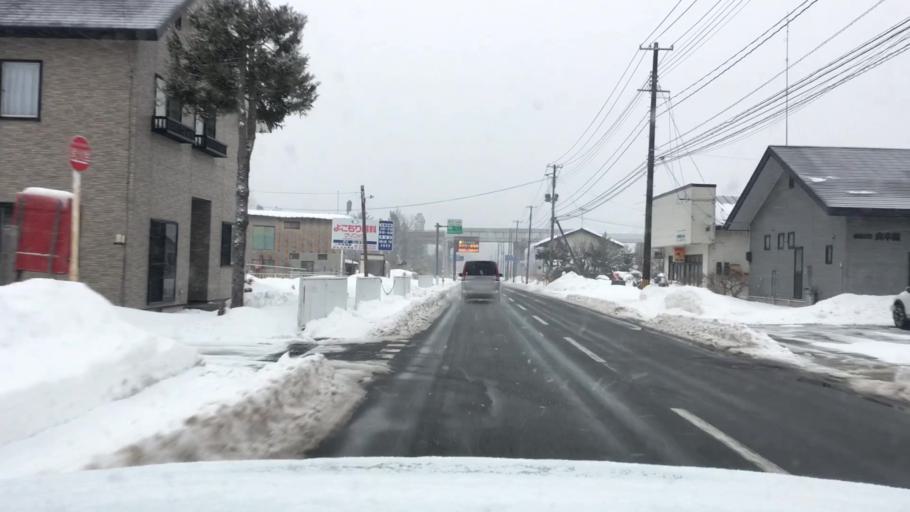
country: JP
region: Iwate
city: Ichinohe
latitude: 40.1072
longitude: 141.0508
